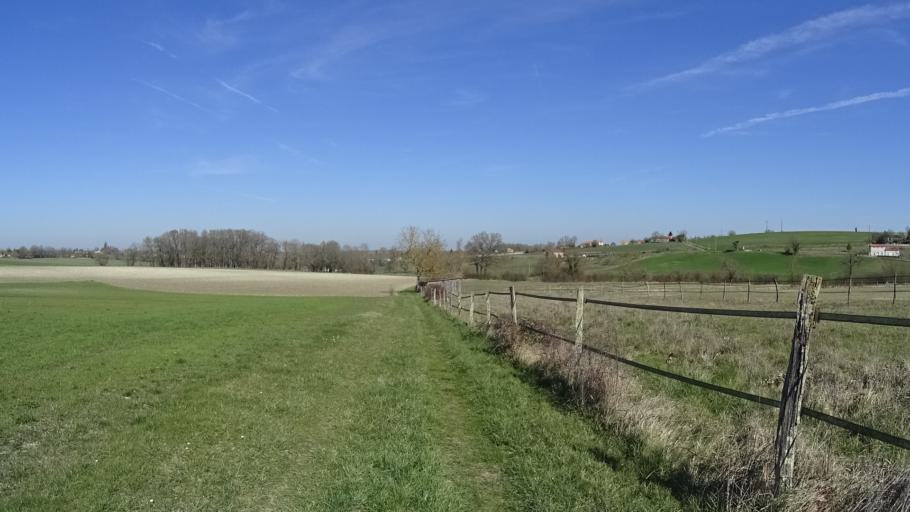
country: FR
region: Aquitaine
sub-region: Departement de la Dordogne
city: Riberac
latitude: 45.2238
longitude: 0.3320
